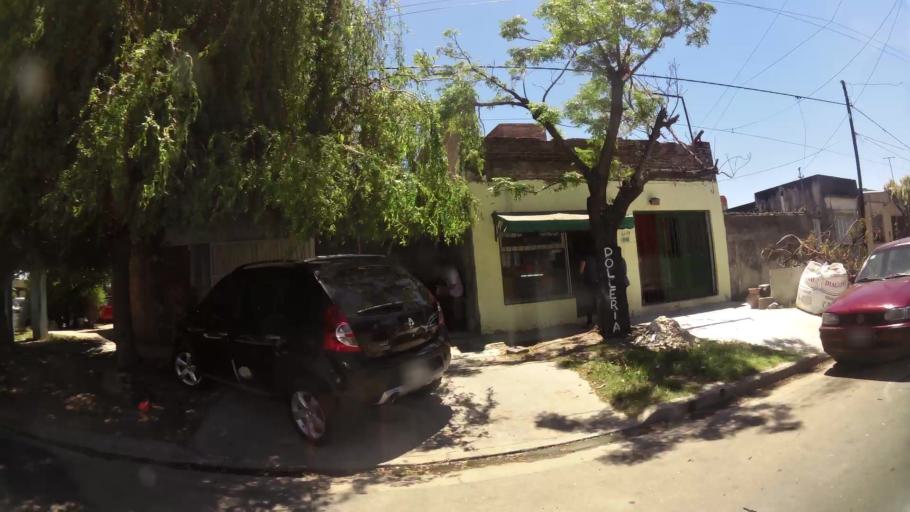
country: AR
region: Santa Fe
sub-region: Departamento de Rosario
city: Rosario
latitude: -32.9545
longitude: -60.7095
